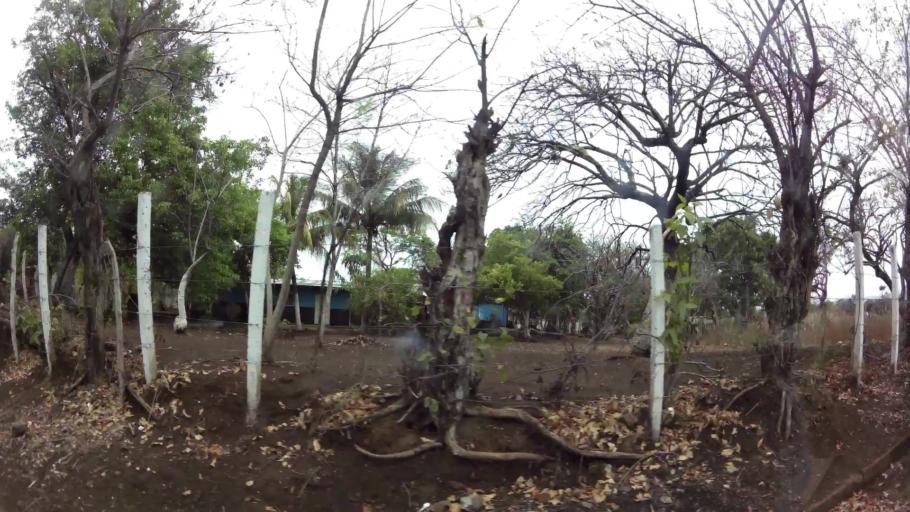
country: NI
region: Granada
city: Nandaime
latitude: 11.7569
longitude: -86.0584
